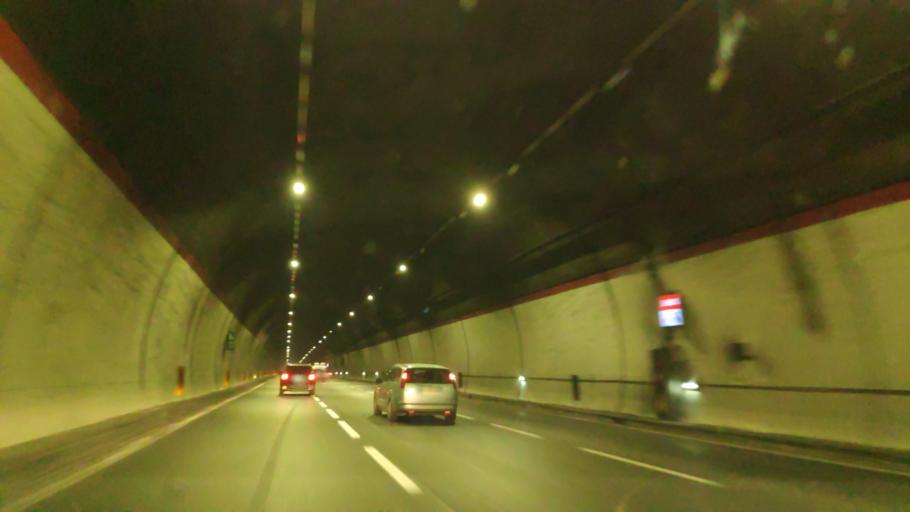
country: IT
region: Campania
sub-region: Provincia di Salerno
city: Pezzano-Filetta
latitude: 40.6716
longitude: 14.8583
